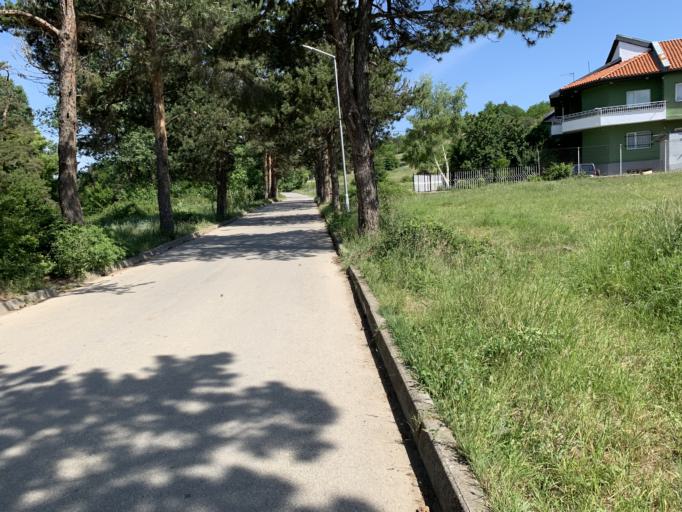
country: AL
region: Korce
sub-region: Rrethi i Korces
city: Korce
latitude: 40.6136
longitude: 20.7896
